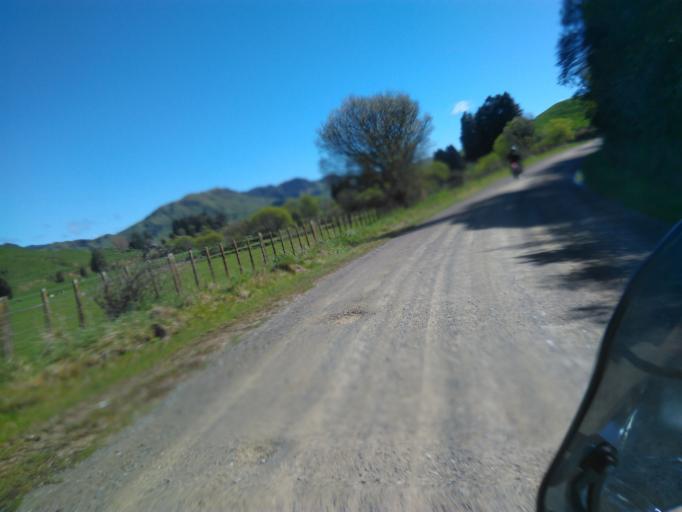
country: NZ
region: Bay of Plenty
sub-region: Opotiki District
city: Opotiki
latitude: -38.2884
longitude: 177.5442
